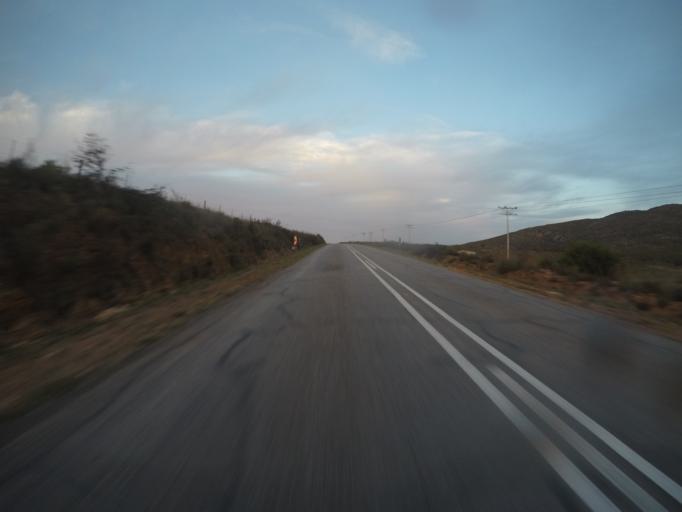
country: ZA
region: Western Cape
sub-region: Eden District Municipality
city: Plettenberg Bay
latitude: -33.7432
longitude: 23.4499
